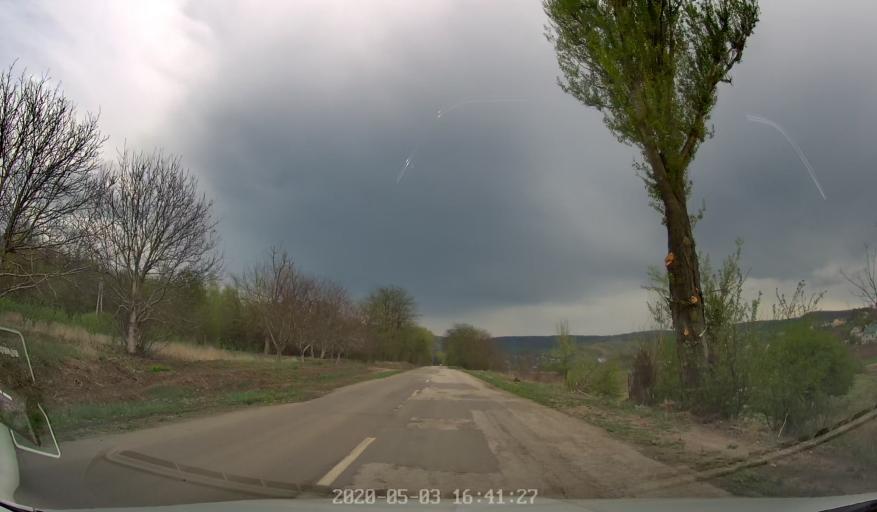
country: MD
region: Stinga Nistrului
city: Bucovat
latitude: 47.1668
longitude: 28.4084
